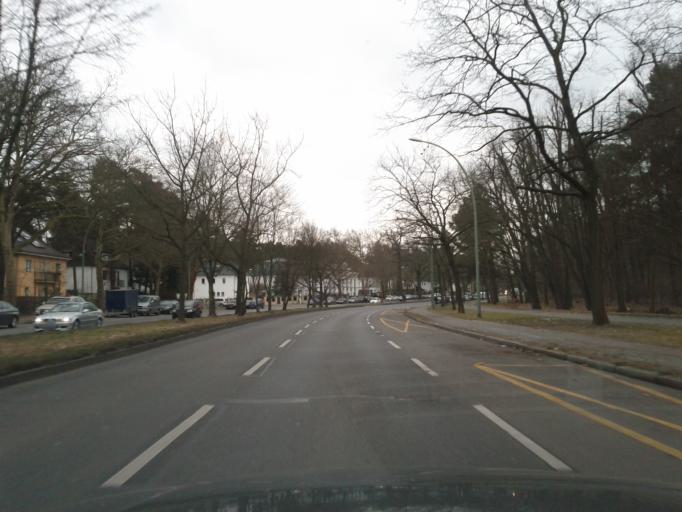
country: DE
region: Berlin
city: Dahlem
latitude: 52.4671
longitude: 13.2783
